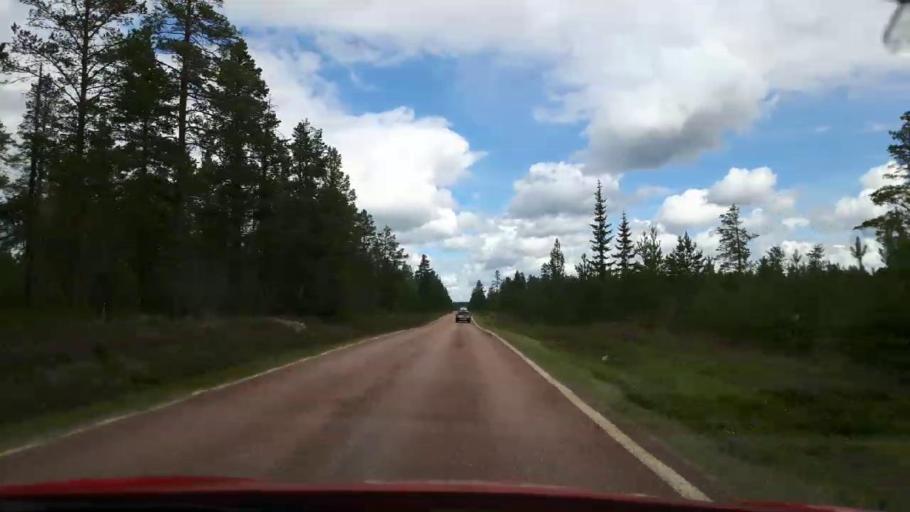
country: NO
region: Hedmark
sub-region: Trysil
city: Innbygda
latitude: 61.8821
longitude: 12.9731
